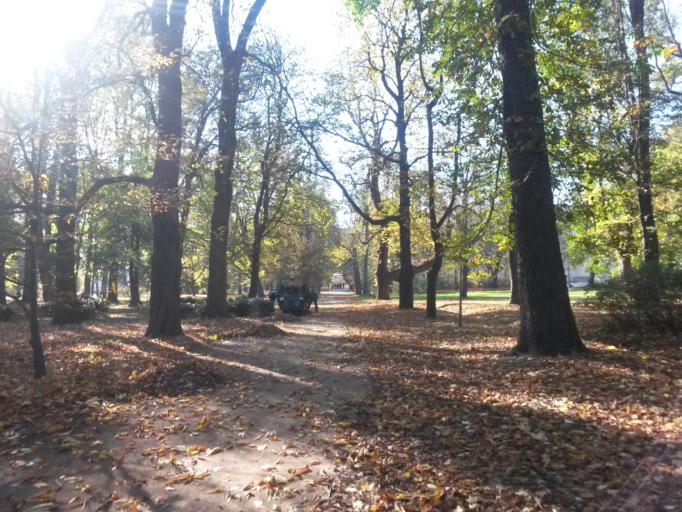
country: PL
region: Masovian Voivodeship
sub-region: Warszawa
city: Srodmiescie
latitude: 52.2170
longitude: 21.0323
